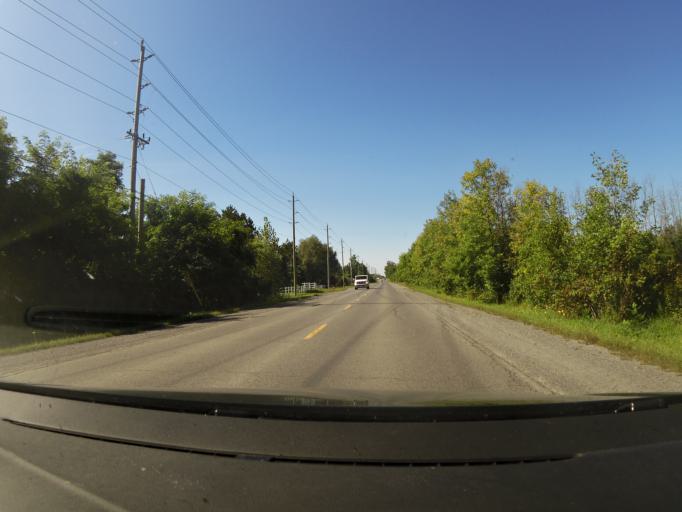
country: CA
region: Ontario
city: Bells Corners
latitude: 45.2991
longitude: -75.9630
